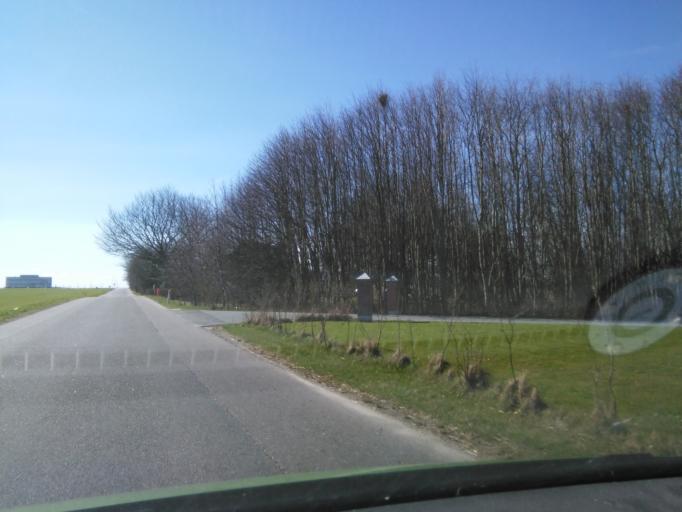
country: DK
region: Central Jutland
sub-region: Favrskov Kommune
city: Soften
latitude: 56.2417
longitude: 10.1049
